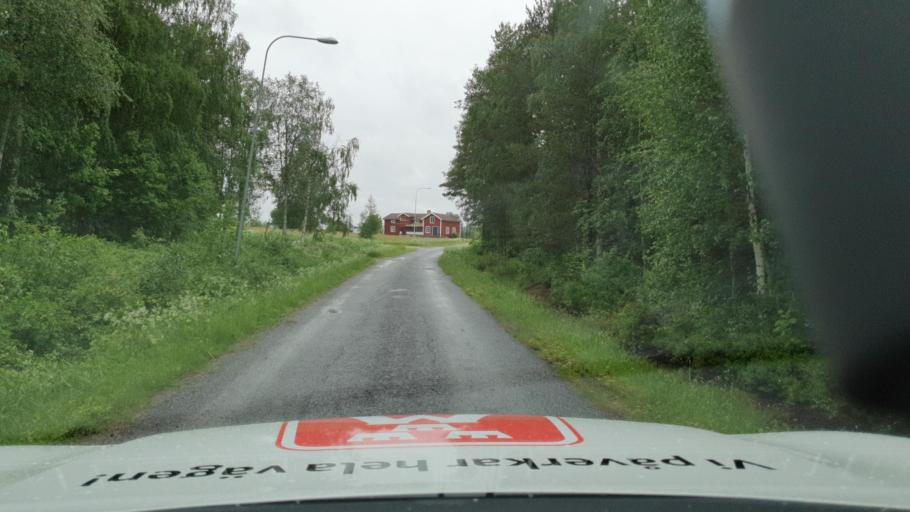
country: SE
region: Vaesterbotten
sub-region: Asele Kommun
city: Asele
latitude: 63.9386
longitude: 17.2770
